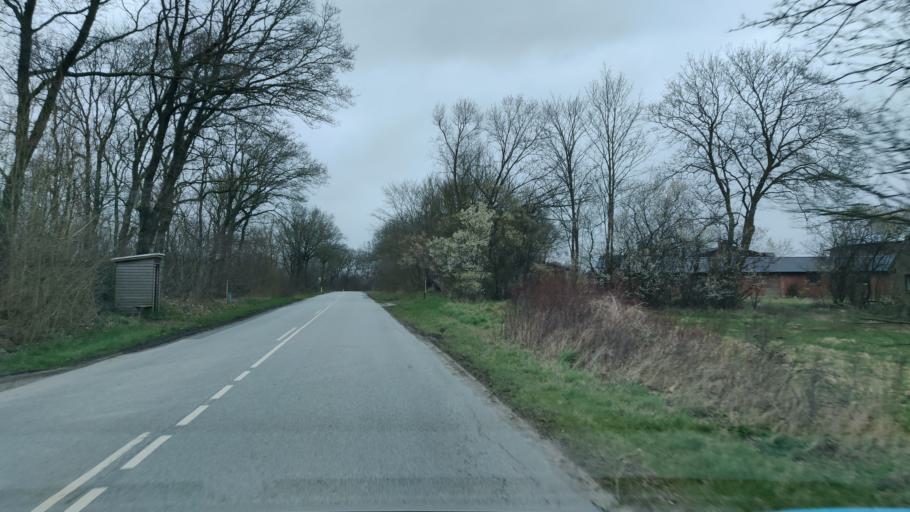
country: DK
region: Central Jutland
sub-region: Skive Kommune
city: Hojslev
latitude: 56.5564
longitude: 9.2476
